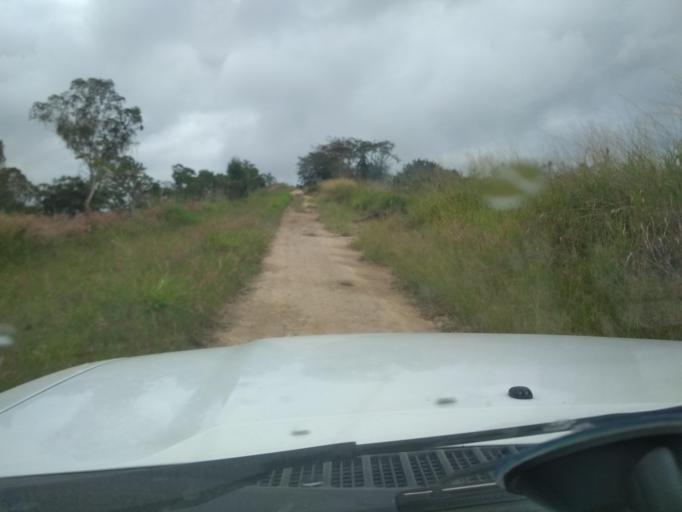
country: MX
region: Veracruz
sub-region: Emiliano Zapata
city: Dos Rios
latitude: 19.5323
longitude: -96.8100
